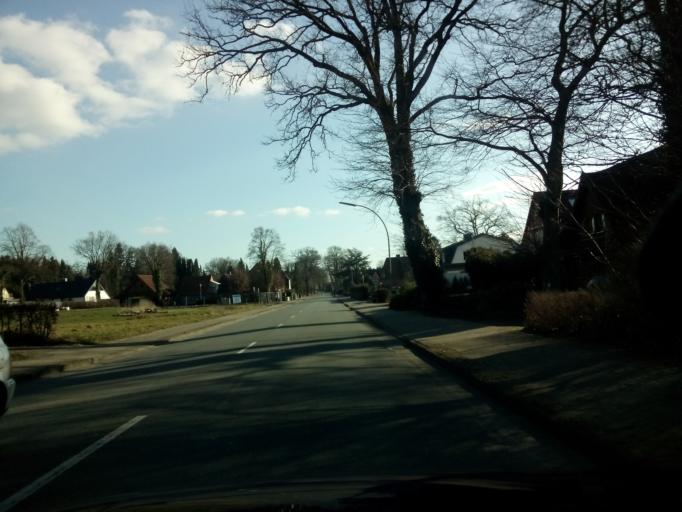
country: DE
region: Lower Saxony
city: Osterholz-Scharmbeck
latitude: 53.2471
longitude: 8.7793
